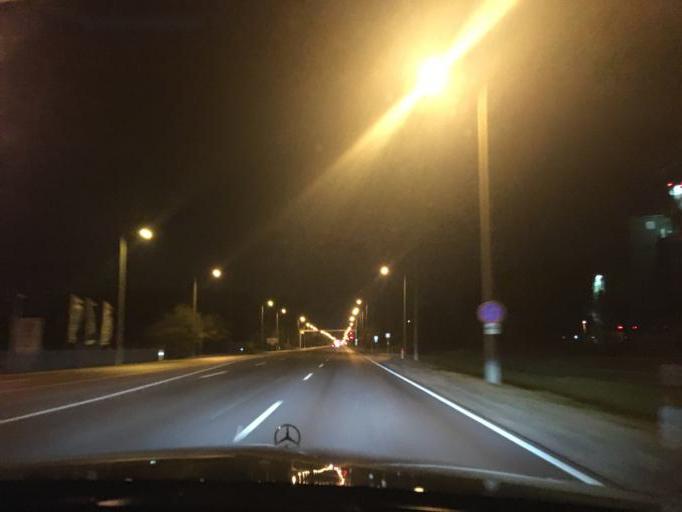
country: HU
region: Hajdu-Bihar
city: Mikepercs
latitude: 47.4869
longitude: 21.6331
